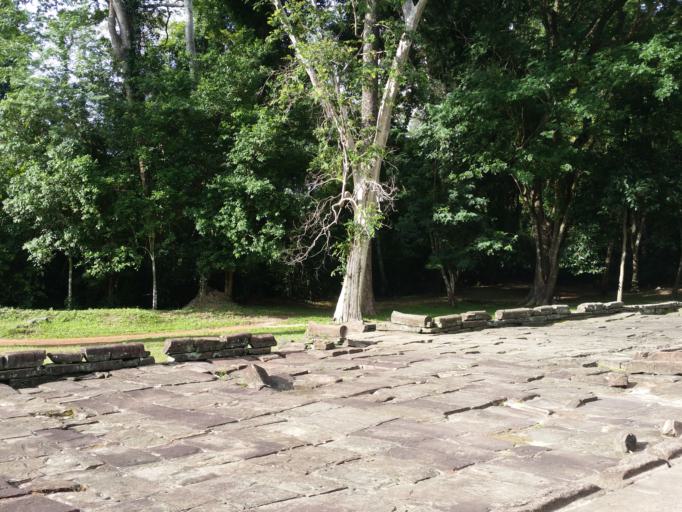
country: KH
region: Siem Reap
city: Siem Reap
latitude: 13.4618
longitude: 103.8729
